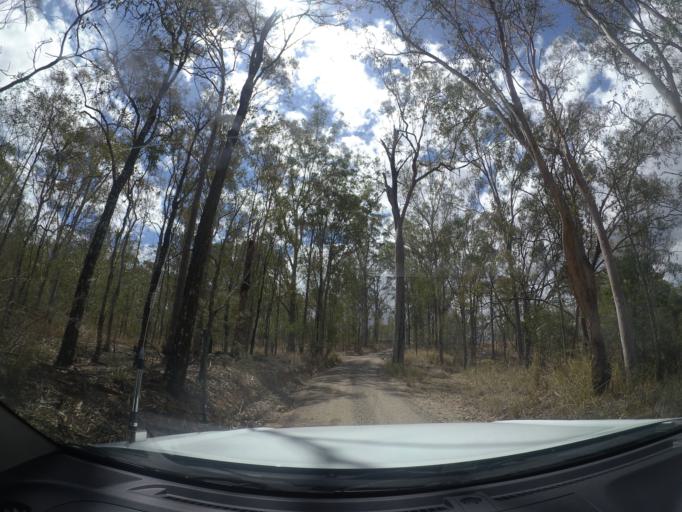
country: AU
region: Queensland
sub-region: Logan
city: Cedar Vale
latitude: -27.8969
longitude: 153.0438
